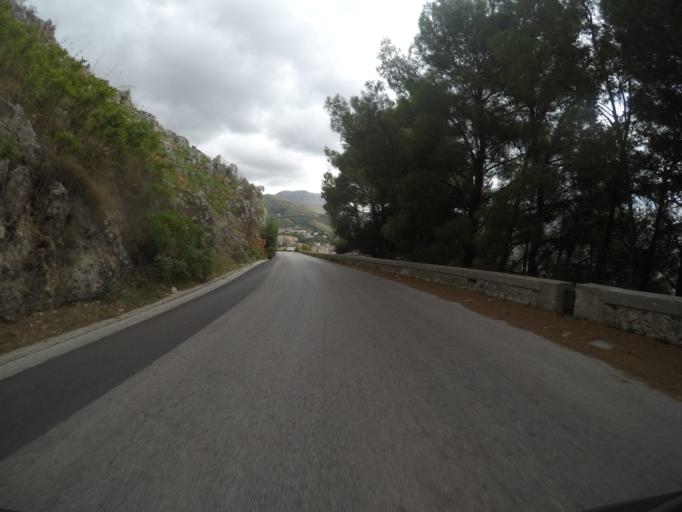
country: IT
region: Sicily
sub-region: Palermo
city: Montelepre
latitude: 38.0955
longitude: 13.1675
